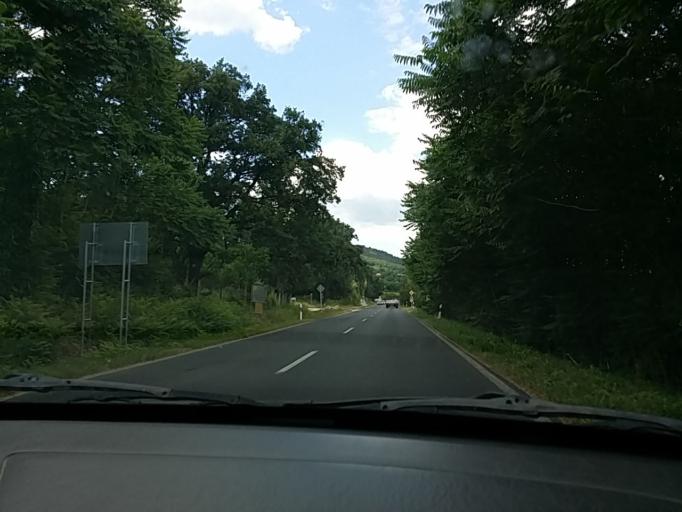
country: HU
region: Veszprem
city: Revfueloep
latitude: 46.8329
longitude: 17.6462
